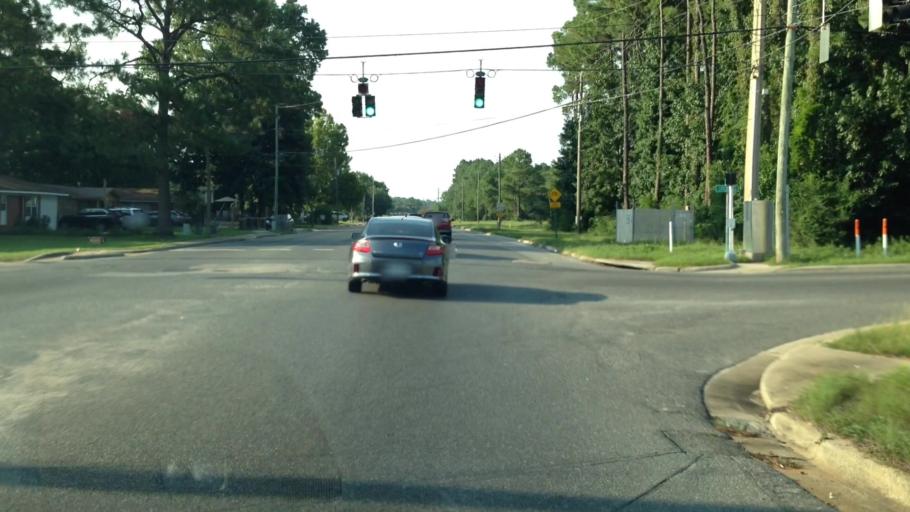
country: US
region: Florida
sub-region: Okaloosa County
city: Mary Esther
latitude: 30.4244
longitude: -86.6673
